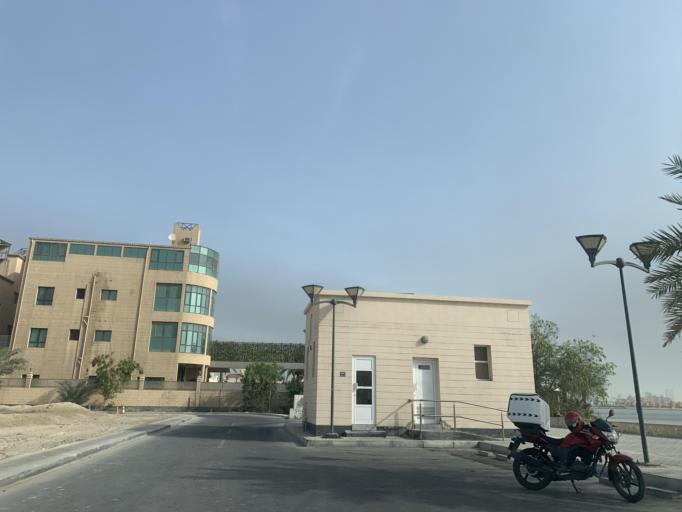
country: BH
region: Northern
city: Madinat `Isa
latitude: 26.1900
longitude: 50.5665
